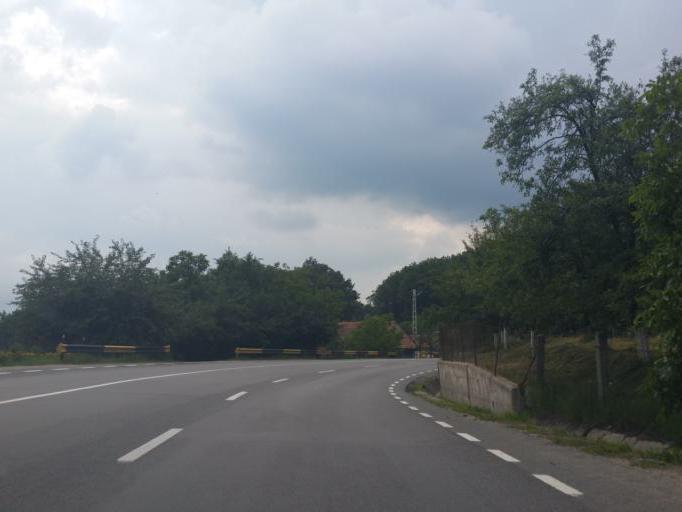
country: RO
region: Salaj
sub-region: Comuna Treznea
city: Treznea
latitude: 47.1349
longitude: 23.1274
